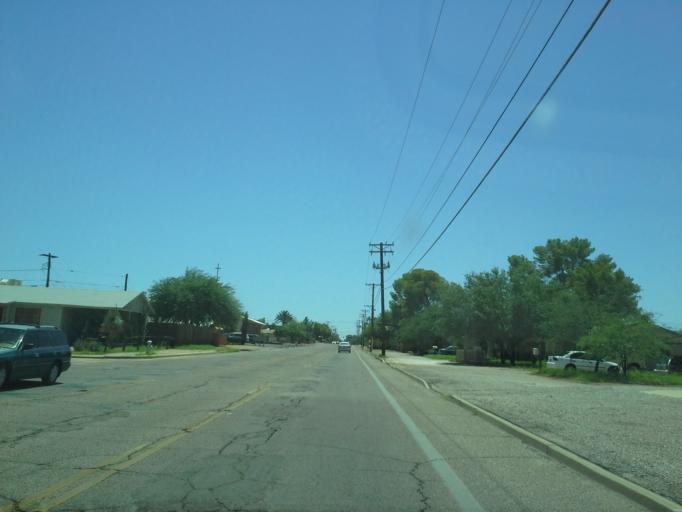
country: US
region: Arizona
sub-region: Pima County
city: Tucson
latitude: 32.2554
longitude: -110.9354
